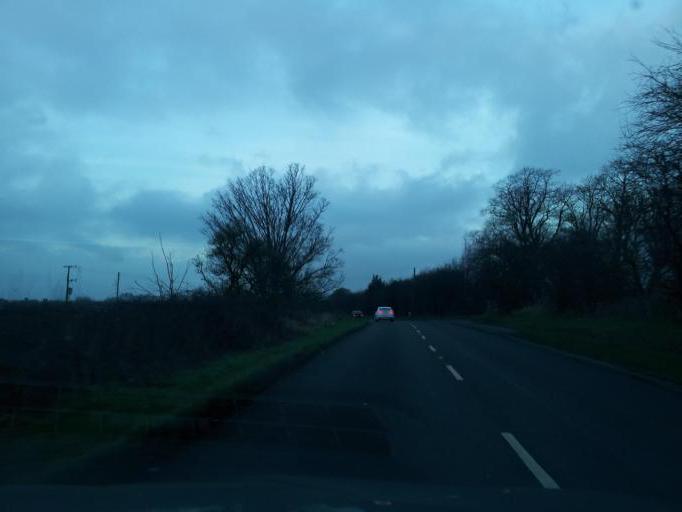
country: GB
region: England
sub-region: Derbyshire
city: Findern
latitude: 52.8604
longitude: -1.5657
